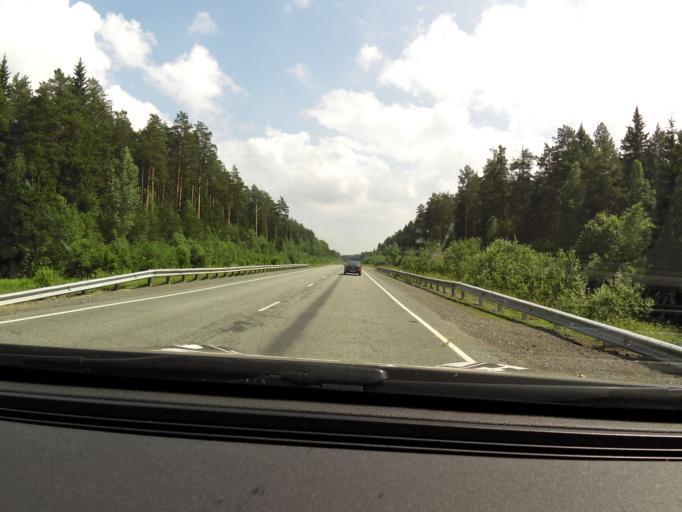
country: RU
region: Sverdlovsk
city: Achit
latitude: 56.8094
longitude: 57.8308
